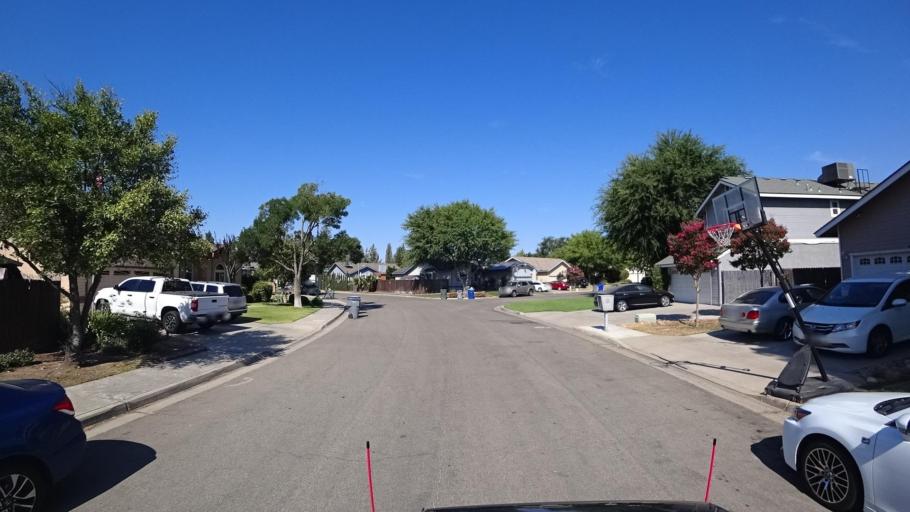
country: US
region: California
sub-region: Fresno County
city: Sunnyside
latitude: 36.7466
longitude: -119.6794
